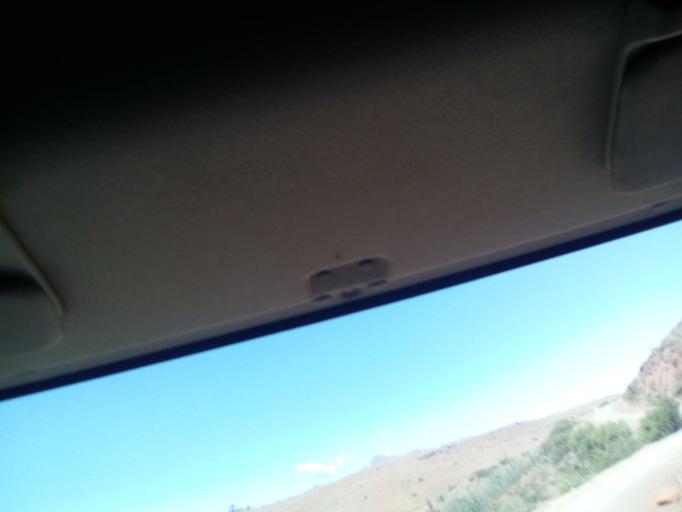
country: LS
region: Qacha's Nek
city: Qacha's Nek
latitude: -30.0580
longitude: 28.6388
